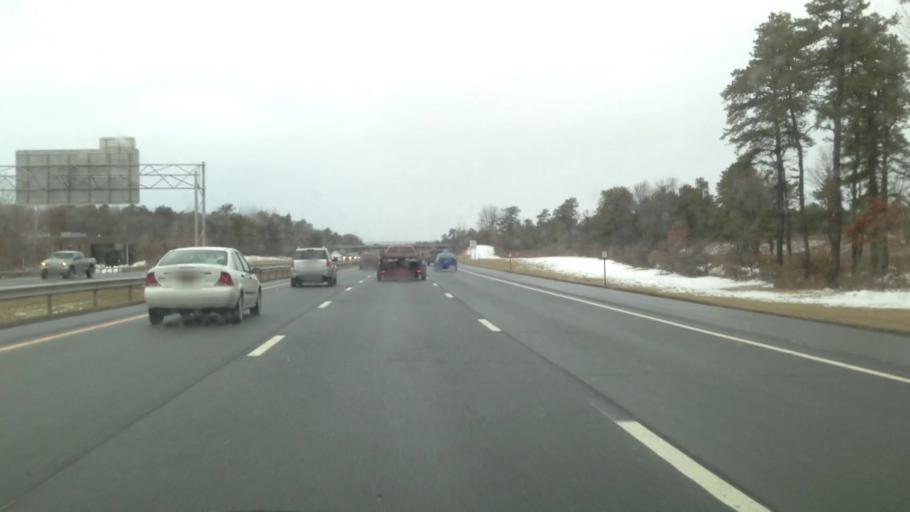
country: US
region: New York
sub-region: Albany County
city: Westmere
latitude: 42.7114
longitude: -73.8641
